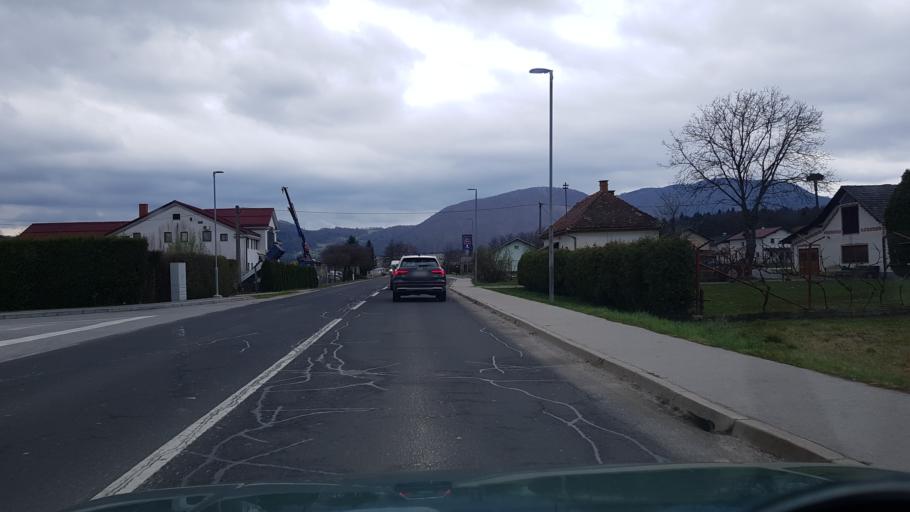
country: SI
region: Slovenska Konjice
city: Slovenske Konjice
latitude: 46.3447
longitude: 15.4738
